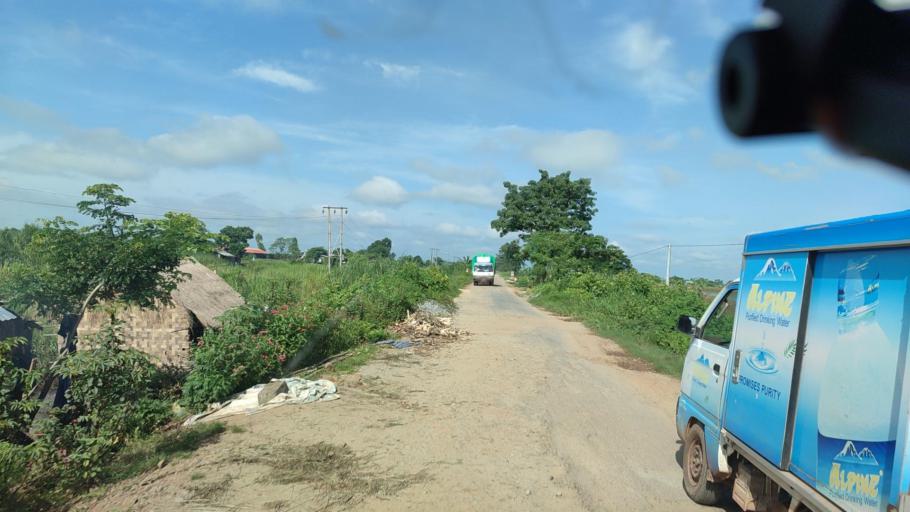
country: MM
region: Bago
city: Letpandan
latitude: 17.7674
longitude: 95.6935
